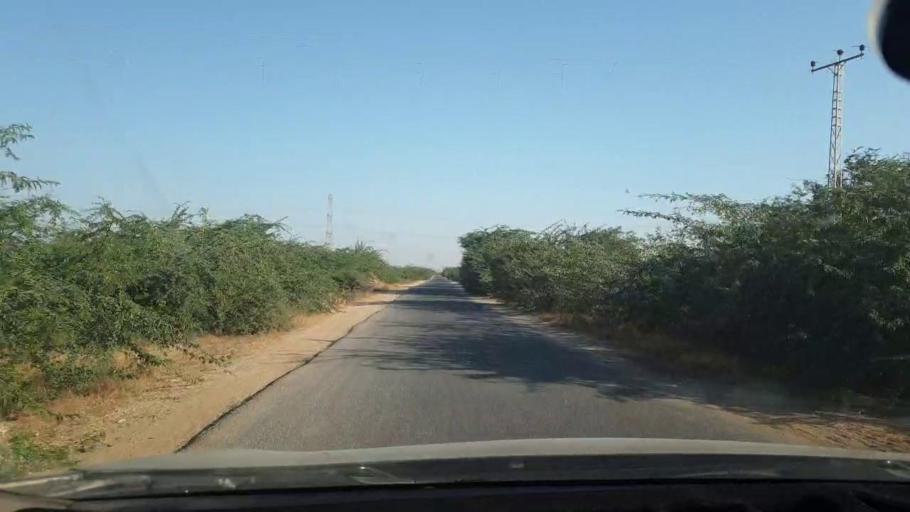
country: PK
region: Sindh
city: Malir Cantonment
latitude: 25.1576
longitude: 67.1928
